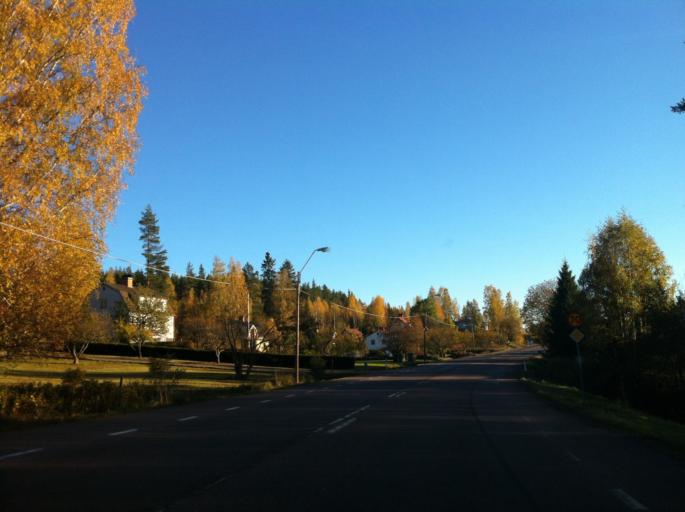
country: SE
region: Dalarna
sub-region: Faluns Kommun
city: Grycksbo
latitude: 60.6993
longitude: 15.4796
